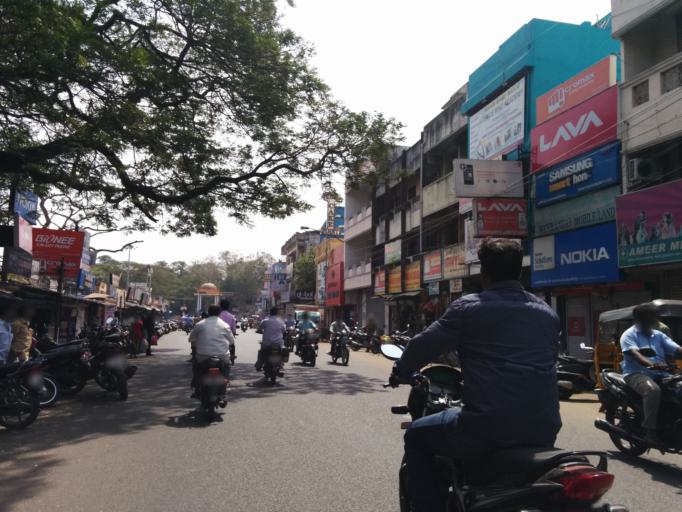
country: IN
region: Pondicherry
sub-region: Puducherry
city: Puducherry
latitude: 11.9317
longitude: 79.8241
